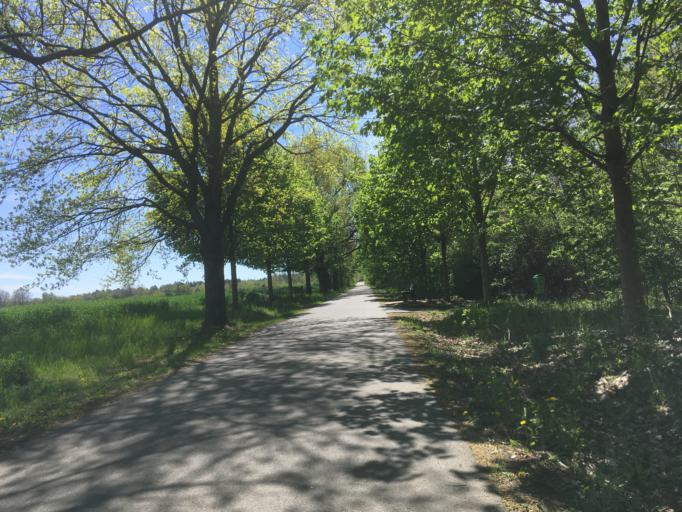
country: DE
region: Brandenburg
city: Wildau
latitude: 52.3137
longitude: 13.6151
